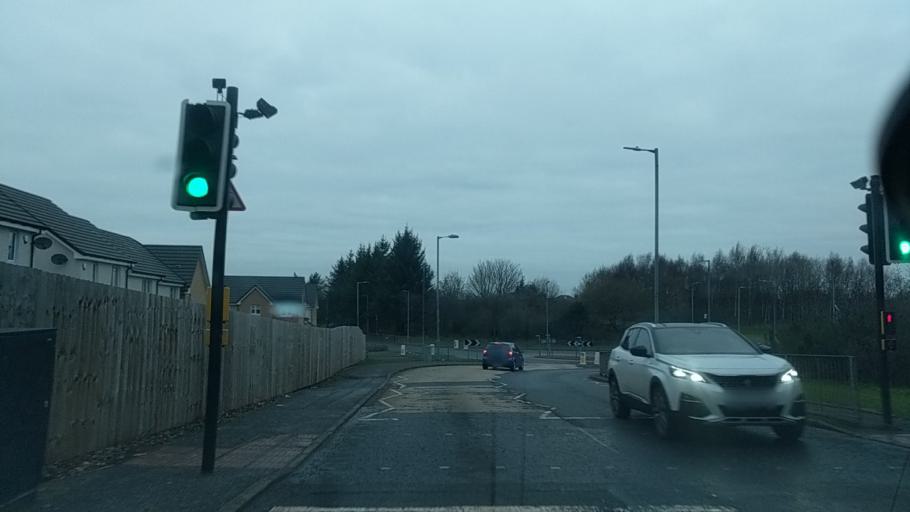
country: GB
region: Scotland
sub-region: South Lanarkshire
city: Rutherglen
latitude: 55.8116
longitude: -4.1848
